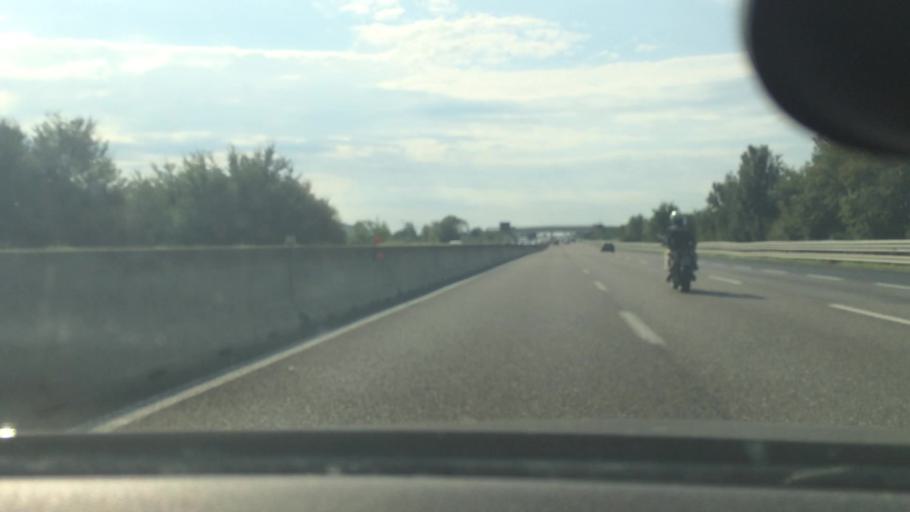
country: IT
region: Emilia-Romagna
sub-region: Provincia di Piacenza
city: Piacenza
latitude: 45.0423
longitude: 9.7572
